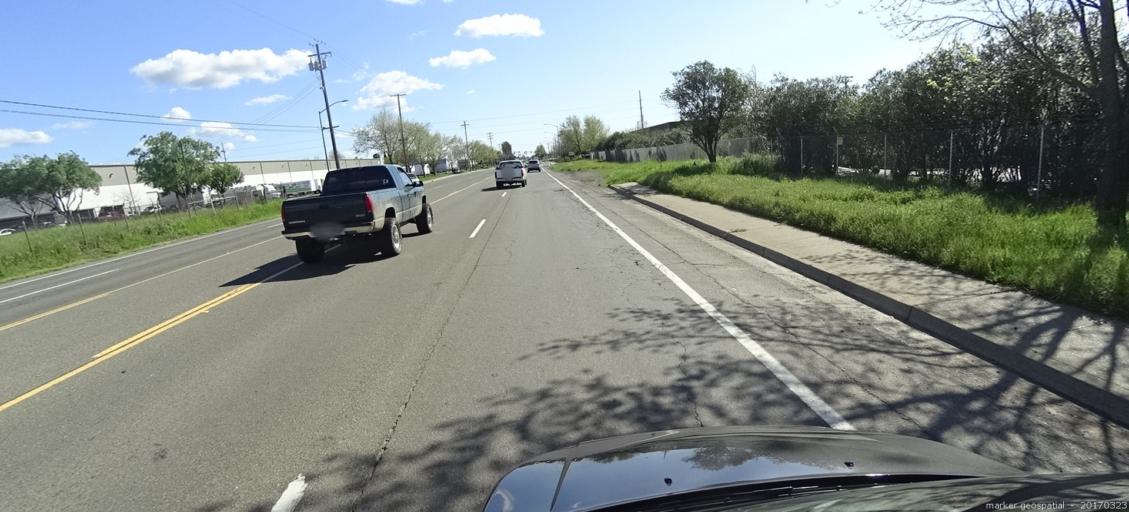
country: US
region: California
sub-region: Sacramento County
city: Rosemont
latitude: 38.5354
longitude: -121.3908
